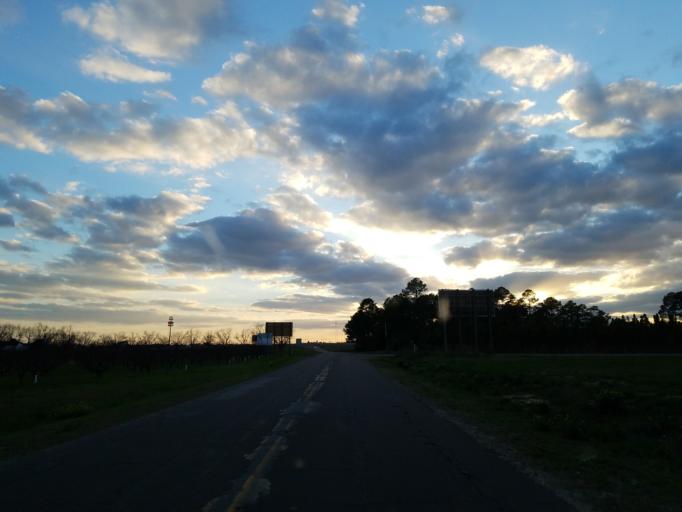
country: US
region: Georgia
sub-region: Dooly County
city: Vienna
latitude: 32.0906
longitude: -83.7554
